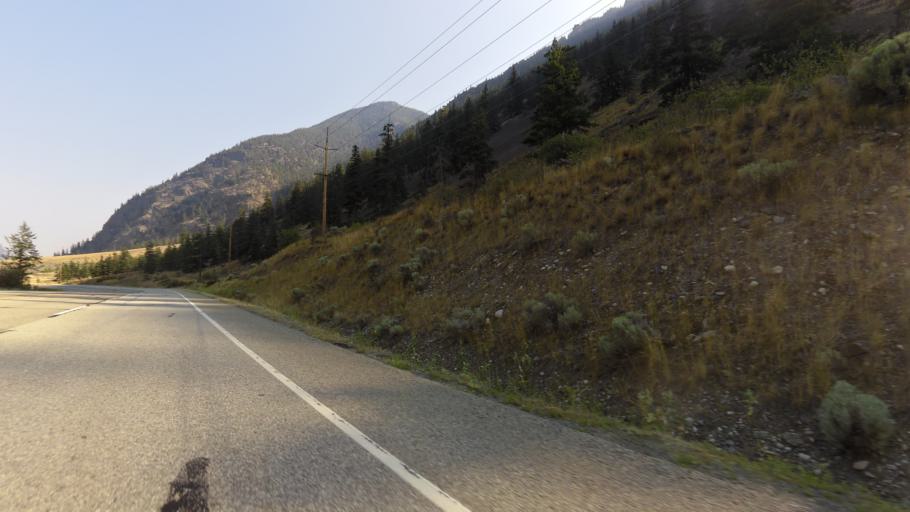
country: CA
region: British Columbia
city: Oliver
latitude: 49.2444
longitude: -120.0033
